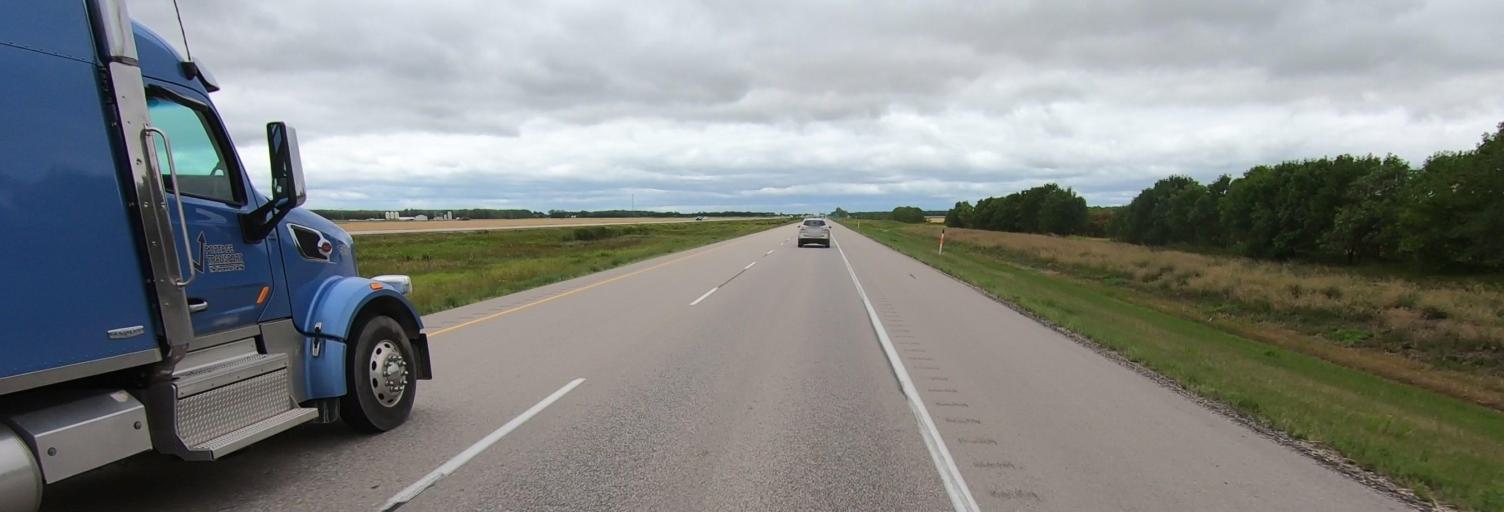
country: CA
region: Manitoba
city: Portage la Prairie
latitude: 49.9472
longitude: -97.9724
